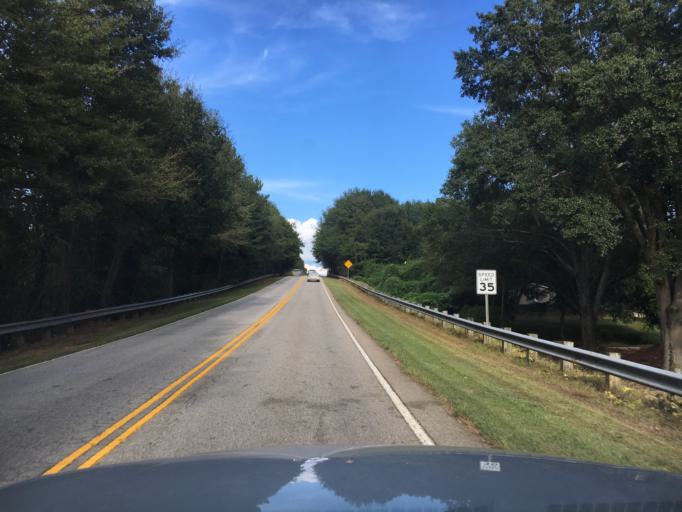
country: US
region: South Carolina
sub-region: Spartanburg County
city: Duncan
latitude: 34.9399
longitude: -82.1407
